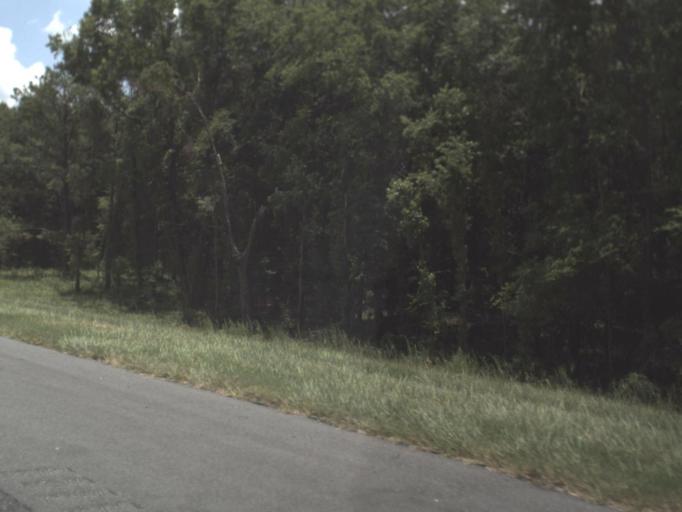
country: US
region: Florida
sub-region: Suwannee County
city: Live Oak
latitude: 30.3587
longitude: -83.1987
